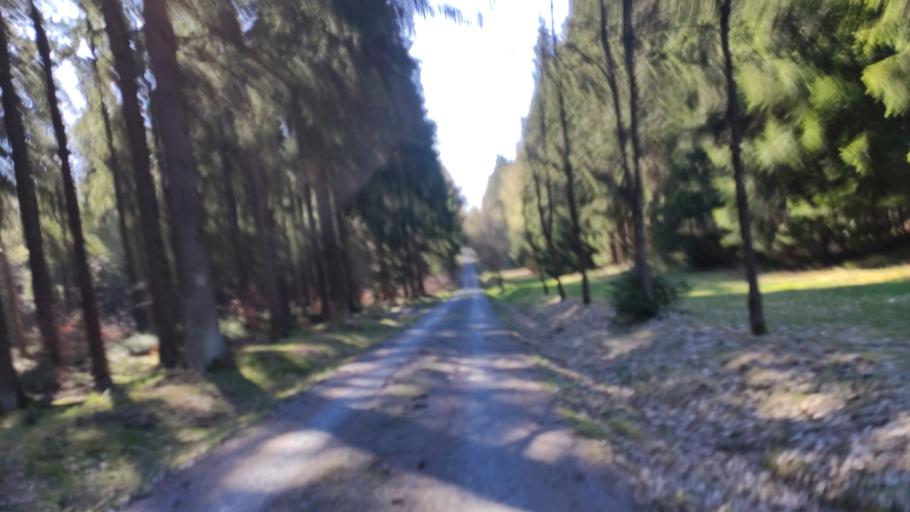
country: DE
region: Bavaria
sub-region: Upper Franconia
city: Reichenbach
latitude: 50.4411
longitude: 11.4468
